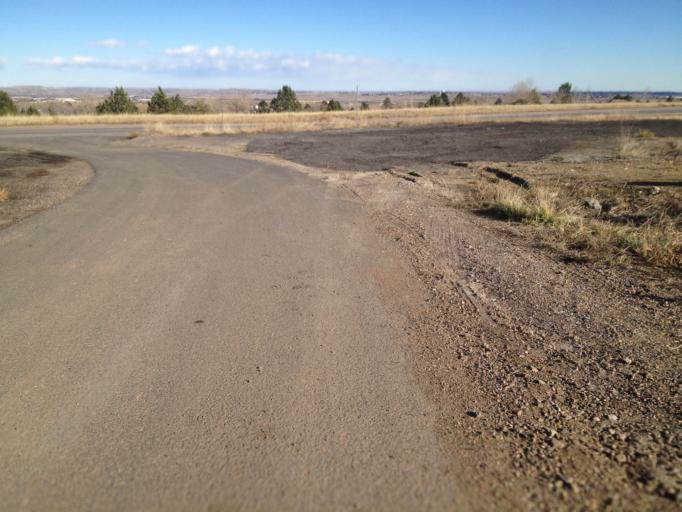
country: US
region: Colorado
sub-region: Boulder County
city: Superior
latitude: 39.9421
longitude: -105.1634
